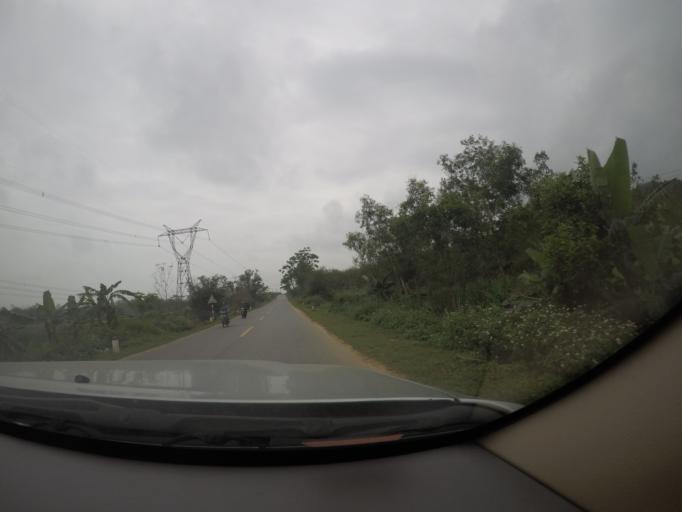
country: VN
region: Quang Binh
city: Hoan Lao
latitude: 17.5474
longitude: 106.4619
